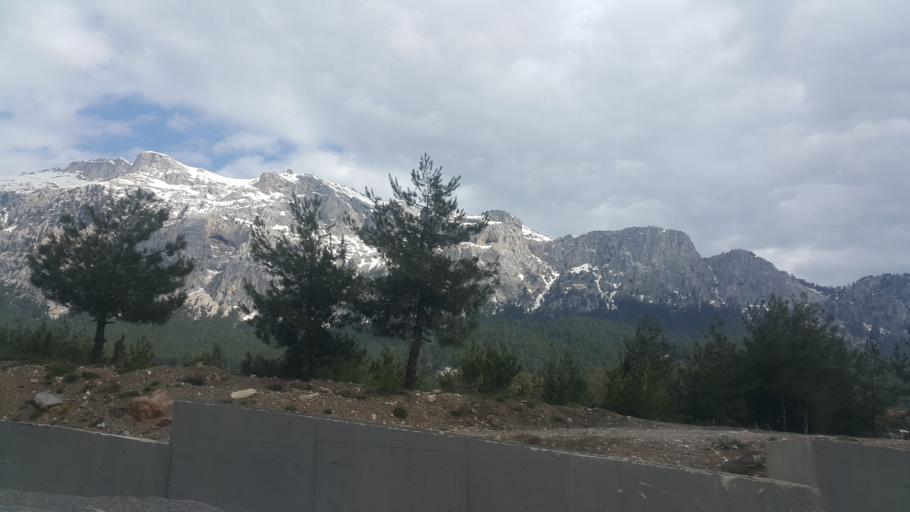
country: TR
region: Adana
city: Pozanti
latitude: 37.3456
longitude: 34.8127
